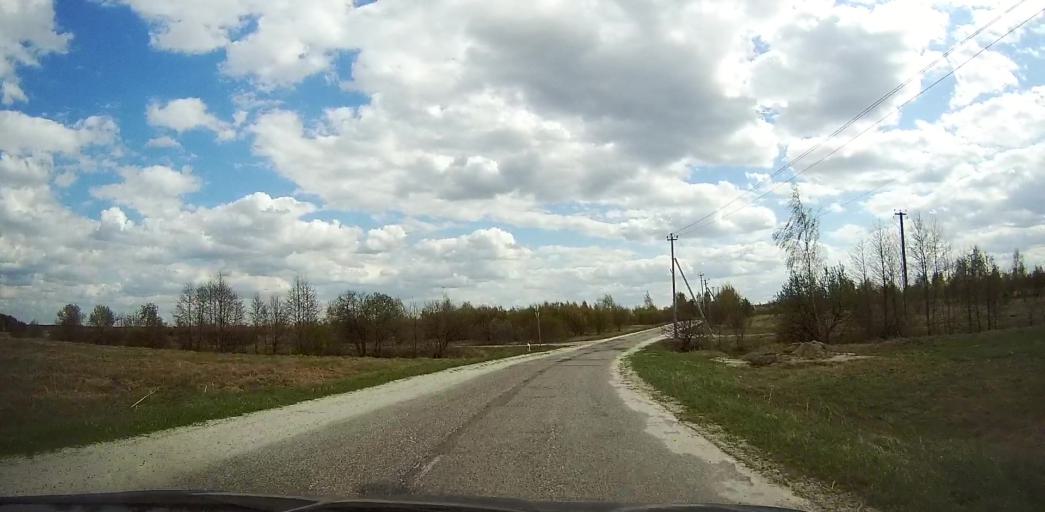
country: RU
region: Moskovskaya
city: Davydovo
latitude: 55.6356
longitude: 38.7823
